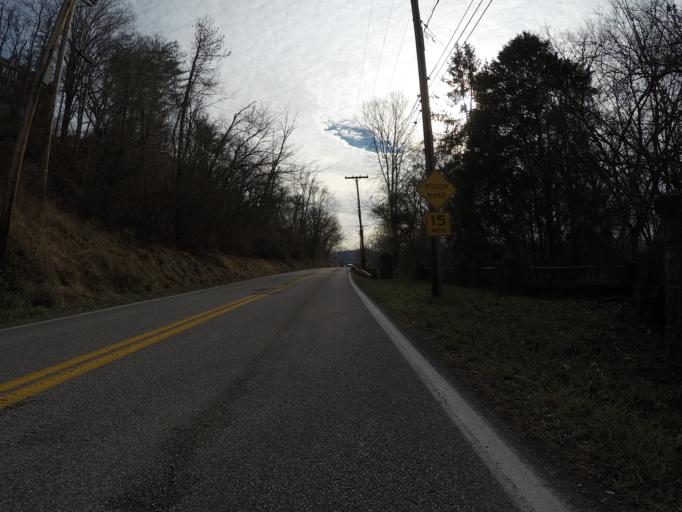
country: US
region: West Virginia
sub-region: Cabell County
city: Barboursville
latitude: 38.4122
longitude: -82.2953
